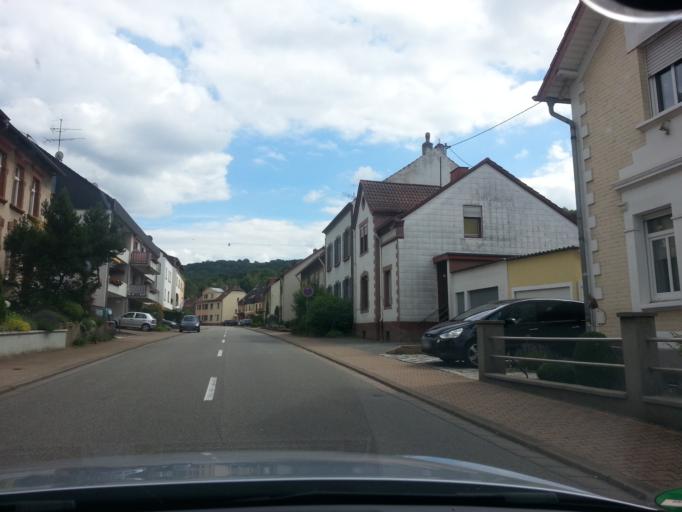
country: DE
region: Saarland
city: Merzig
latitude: 49.4432
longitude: 6.6521
